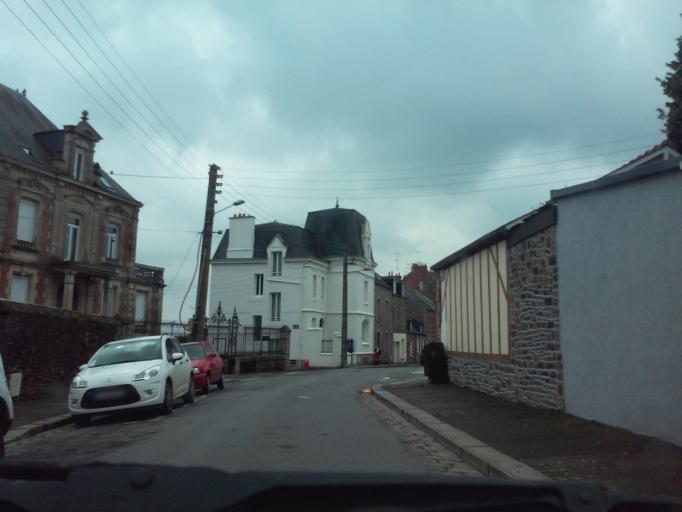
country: FR
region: Brittany
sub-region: Departement d'Ille-et-Vilaine
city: Fougeres
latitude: 48.3572
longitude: -1.1928
